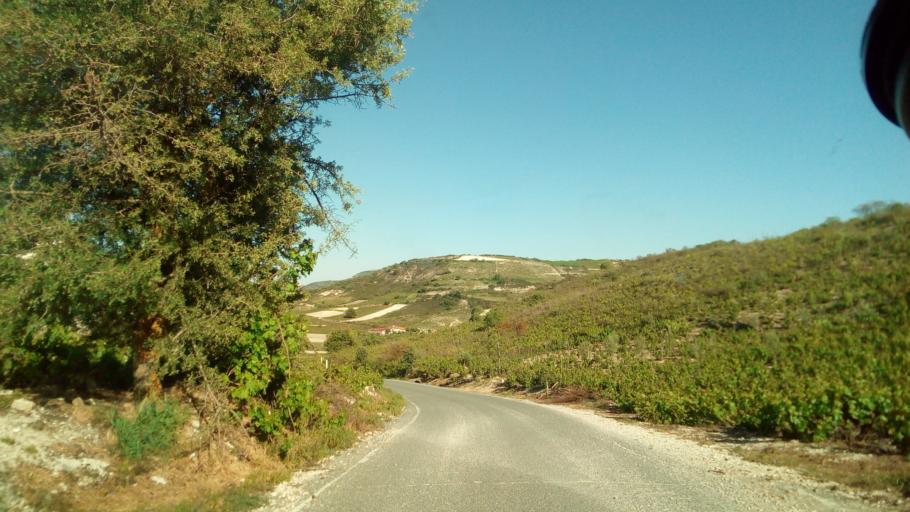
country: CY
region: Limassol
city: Pachna
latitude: 34.8644
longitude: 32.7880
